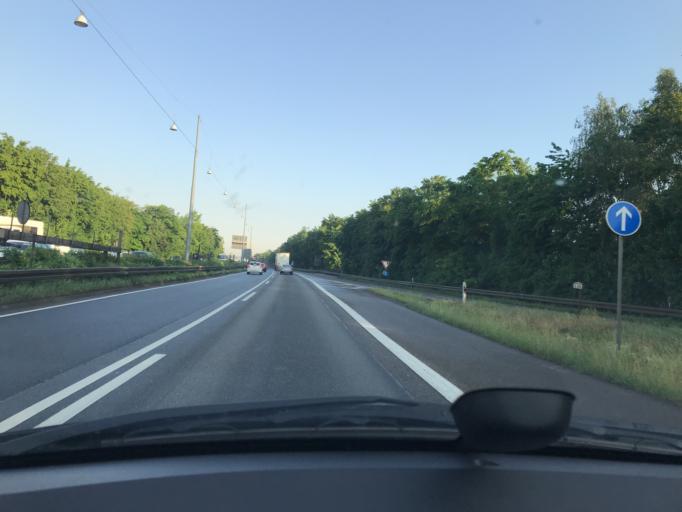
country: DE
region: Saarland
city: Saarbrucken
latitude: 49.2219
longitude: 7.0136
